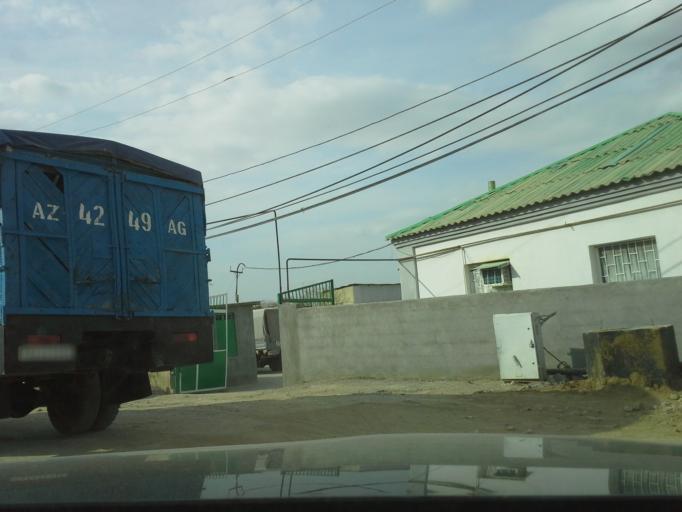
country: TM
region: Ahal
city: Abadan
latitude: 37.9600
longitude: 58.2099
